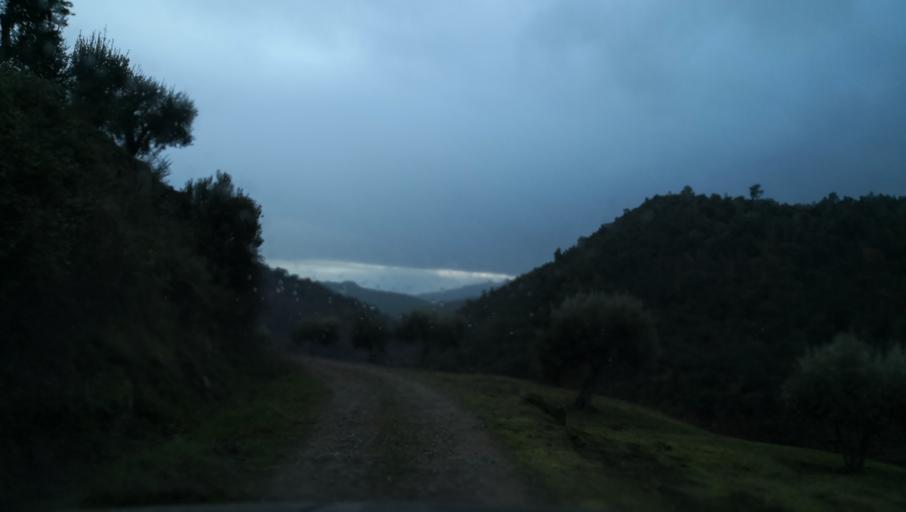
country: PT
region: Vila Real
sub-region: Santa Marta de Penaguiao
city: Santa Marta de Penaguiao
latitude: 41.2205
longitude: -7.7564
